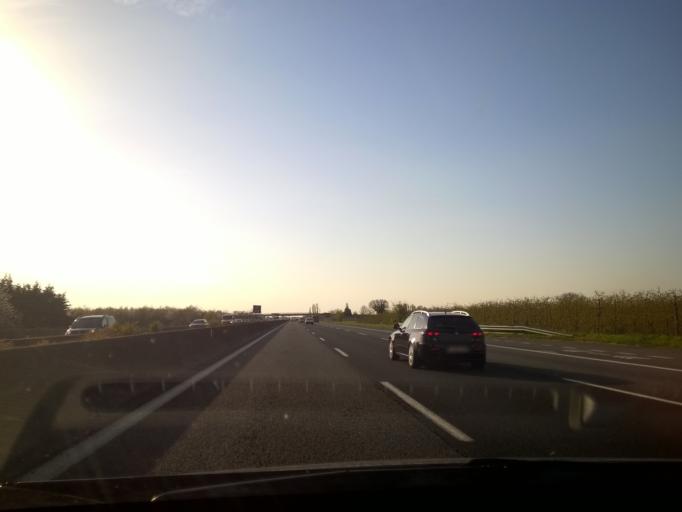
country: IT
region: Emilia-Romagna
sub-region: Provincia di Bologna
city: Castel Guelfo di Bologna
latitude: 44.4065
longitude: 11.6749
